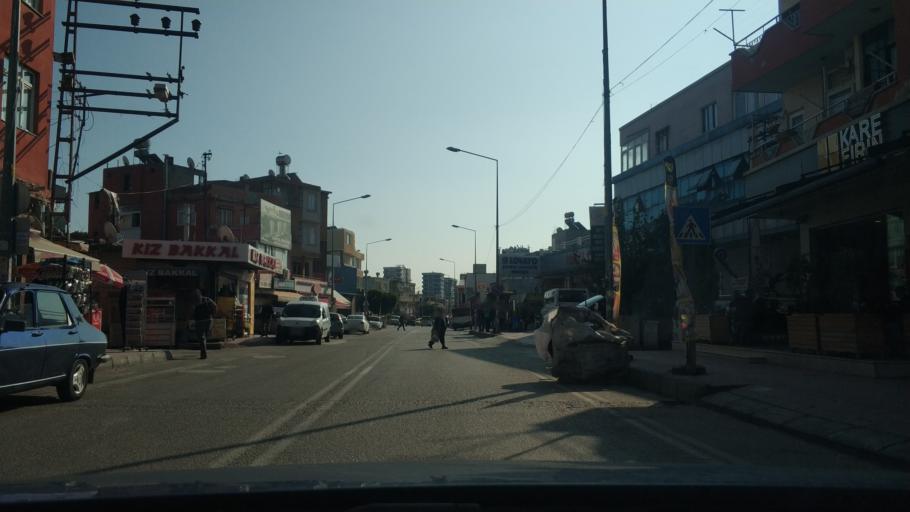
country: TR
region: Adana
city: Seyhan
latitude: 37.0196
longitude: 35.2963
